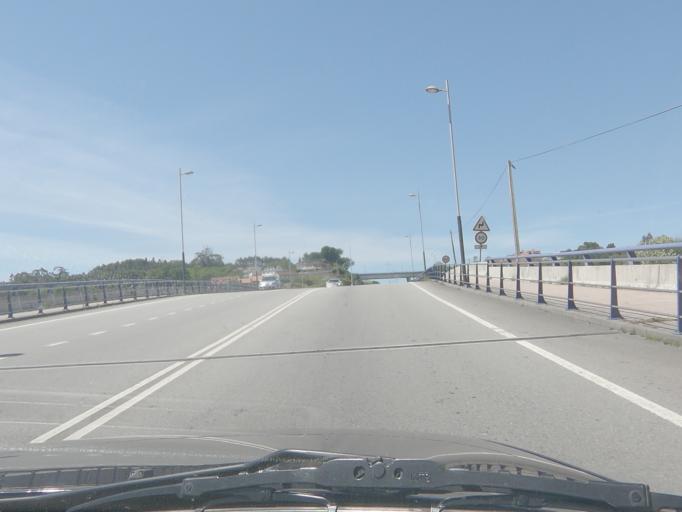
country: ES
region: Galicia
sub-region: Provincia de Pontevedra
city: Pontevedra
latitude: 42.4161
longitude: -8.6346
